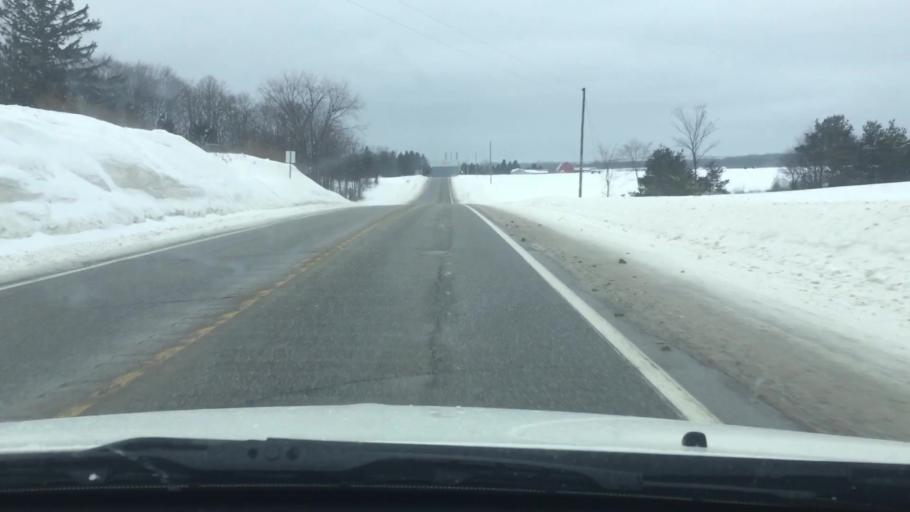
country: US
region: Michigan
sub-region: Charlevoix County
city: Boyne City
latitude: 45.0665
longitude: -84.8815
